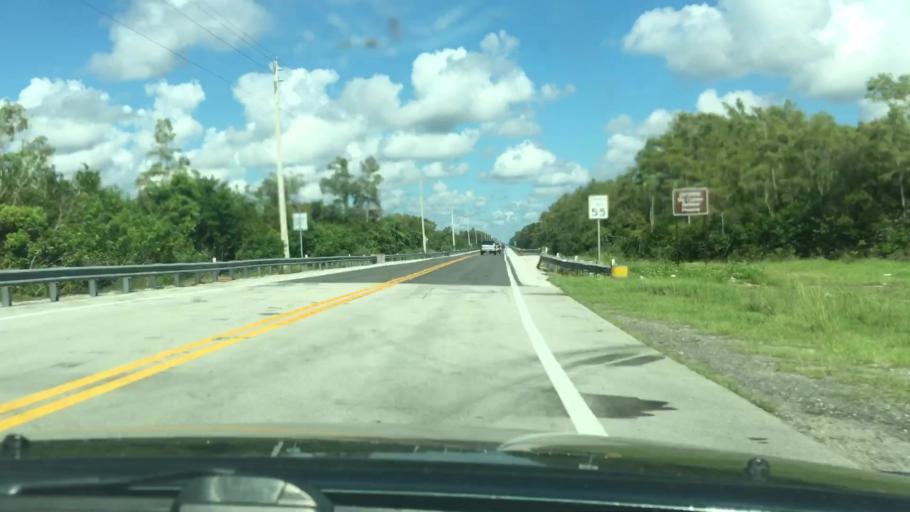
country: US
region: Florida
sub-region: Miami-Dade County
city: Kendall West
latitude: 25.7634
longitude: -80.8299
